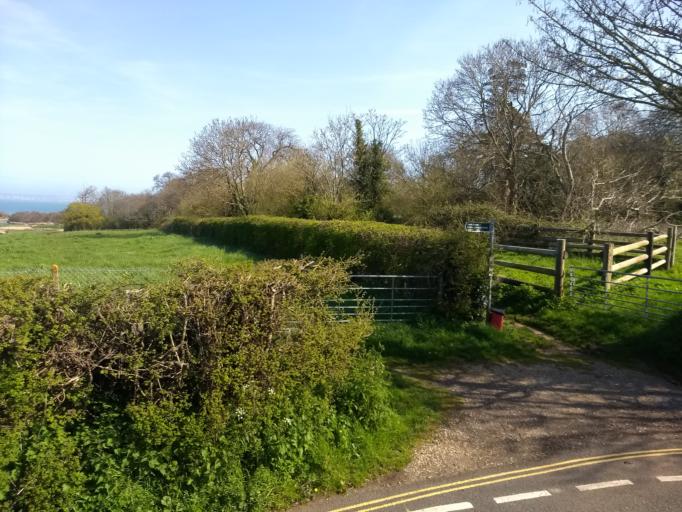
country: GB
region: England
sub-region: Isle of Wight
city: Seaview
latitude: 50.7150
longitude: -1.1189
